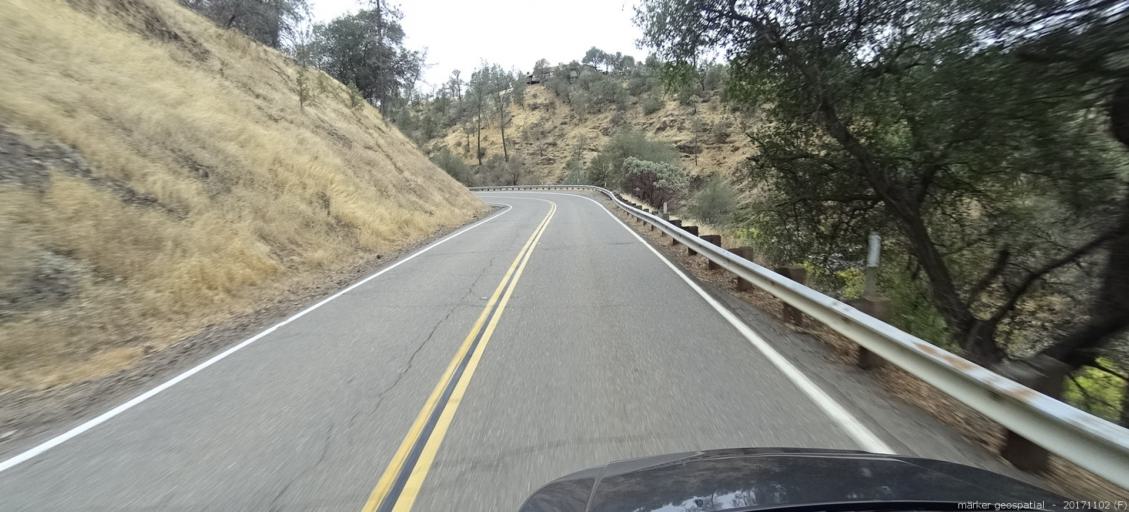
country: US
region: California
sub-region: Shasta County
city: Bella Vista
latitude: 40.6779
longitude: -122.2428
